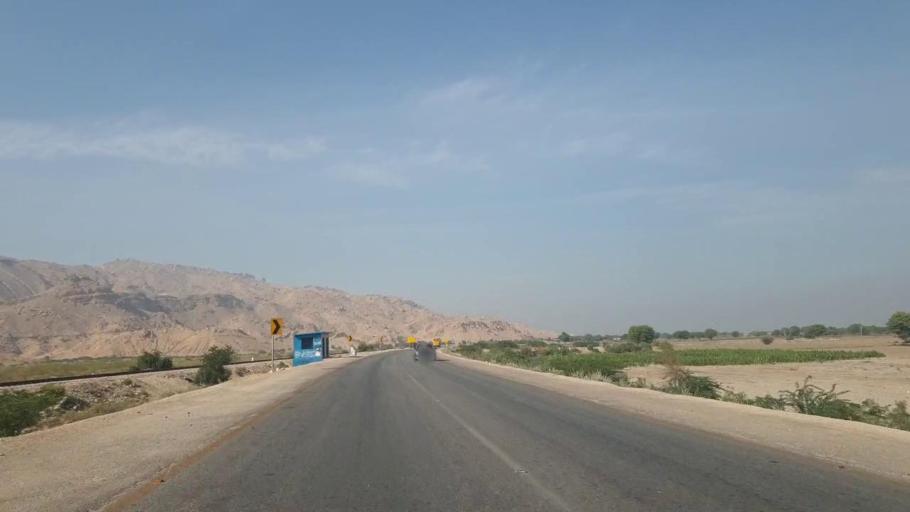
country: PK
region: Sindh
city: Sehwan
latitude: 26.2802
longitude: 67.8966
